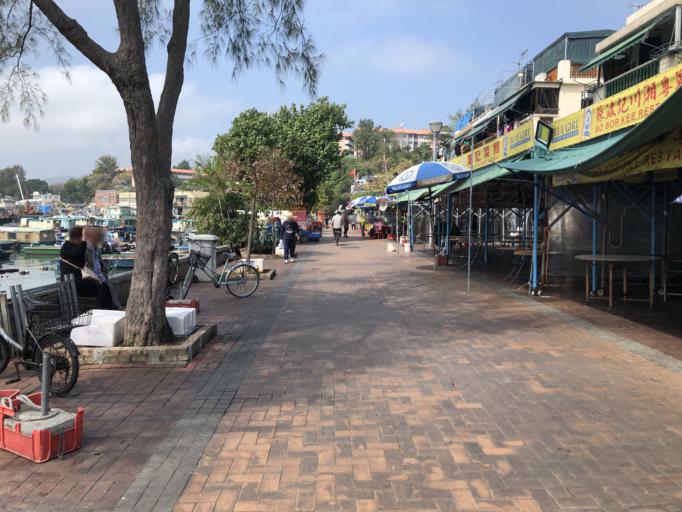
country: HK
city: Yung Shue Wan
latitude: 22.2112
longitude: 114.0274
